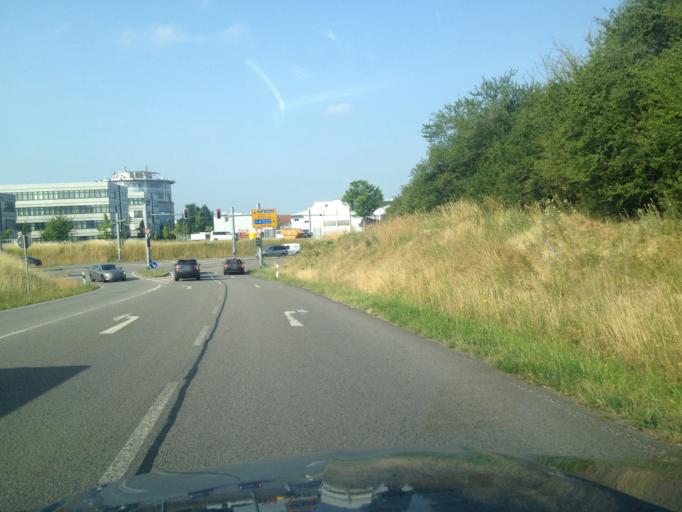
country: DE
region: Baden-Wuerttemberg
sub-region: Karlsruhe Region
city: Walldorf
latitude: 49.2972
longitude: 8.6497
